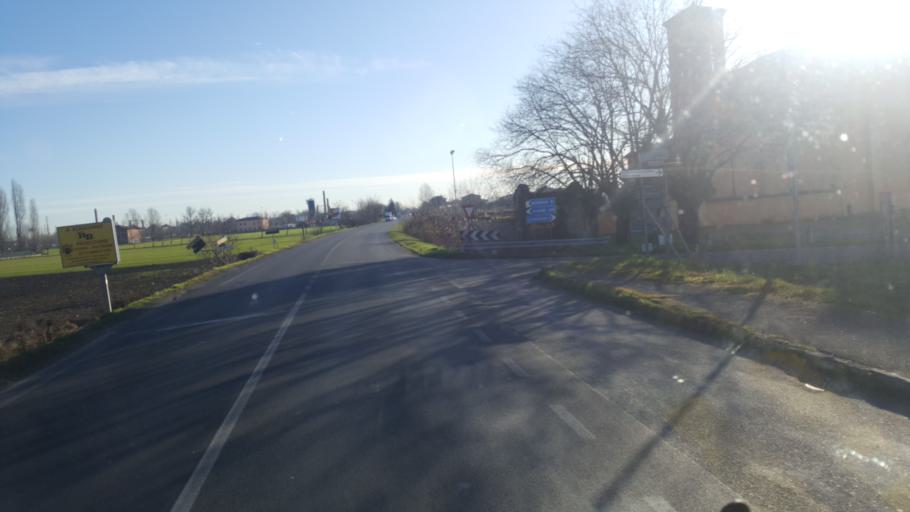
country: IT
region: Emilia-Romagna
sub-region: Provincia di Modena
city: Campogalliano
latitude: 44.6477
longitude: 10.8437
